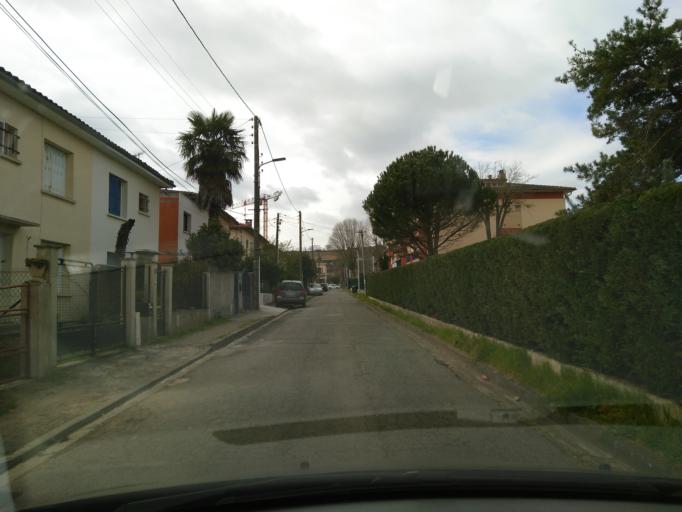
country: FR
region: Midi-Pyrenees
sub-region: Departement de la Haute-Garonne
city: Ramonville-Saint-Agne
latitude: 43.5701
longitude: 1.4579
